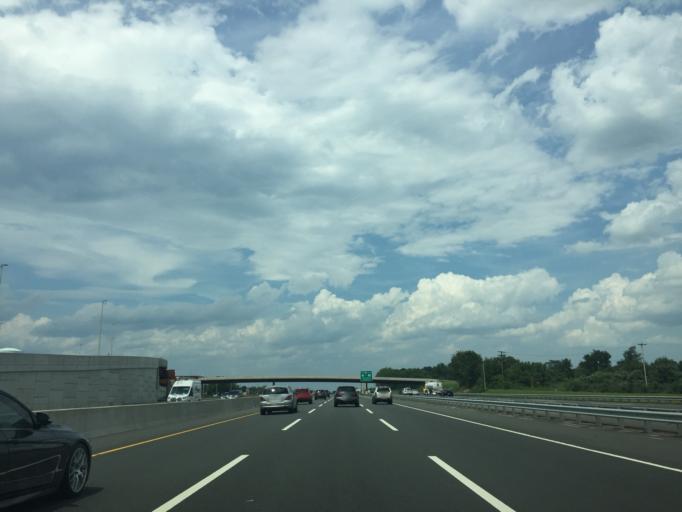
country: US
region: New Jersey
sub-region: Middlesex County
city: Cranbury
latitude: 40.3154
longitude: -74.4889
